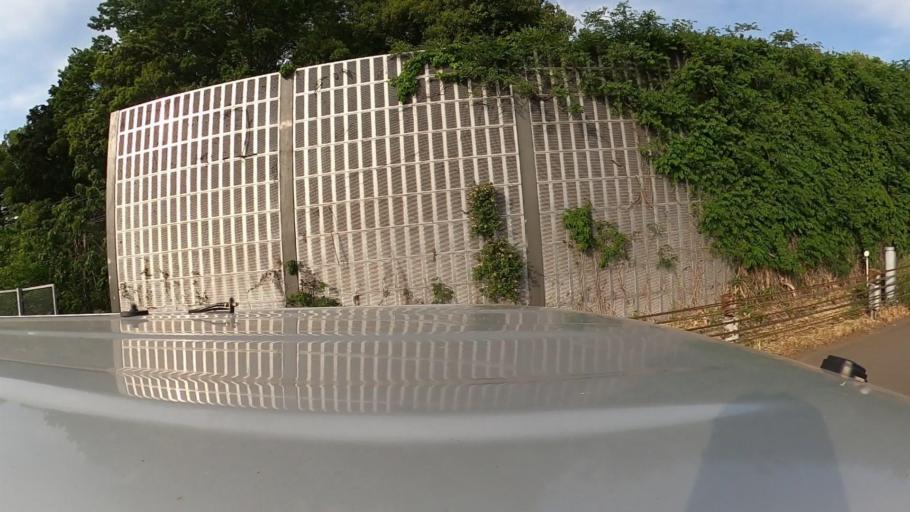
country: JP
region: Saitama
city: Oi
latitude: 35.8189
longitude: 139.5226
